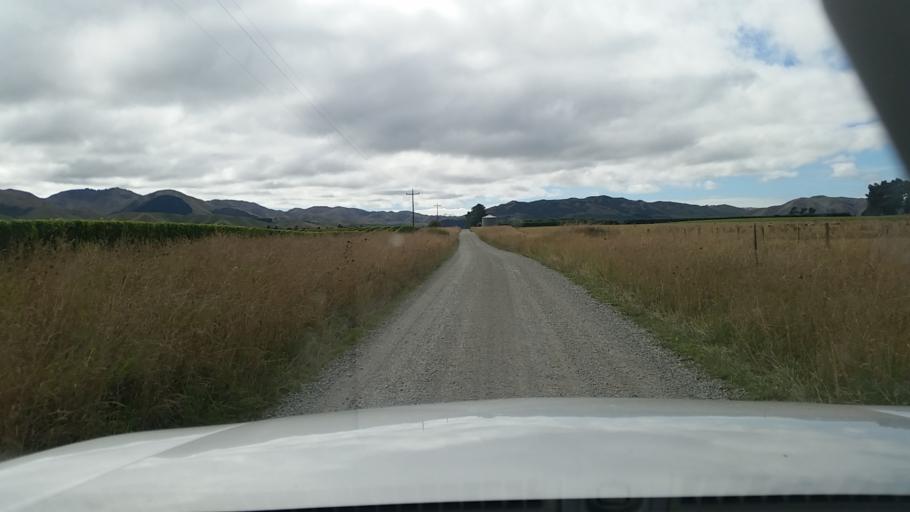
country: NZ
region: Marlborough
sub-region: Marlborough District
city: Blenheim
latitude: -41.6821
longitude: 174.0387
